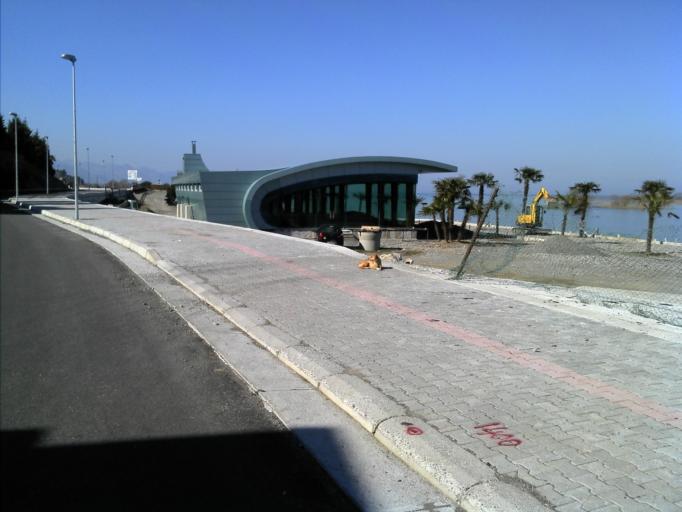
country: AL
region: Shkoder
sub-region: Rrethi i Shkodres
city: Shkoder
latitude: 42.0540
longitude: 19.4785
